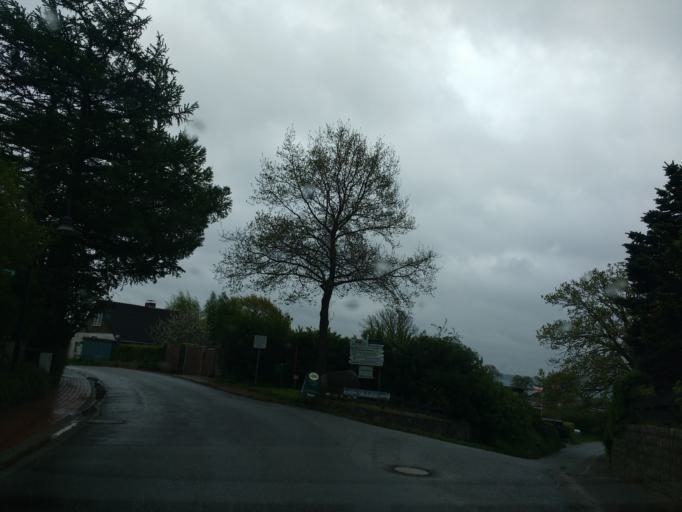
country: DE
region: Schleswig-Holstein
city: Waabs
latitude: 54.5151
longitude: 9.9827
